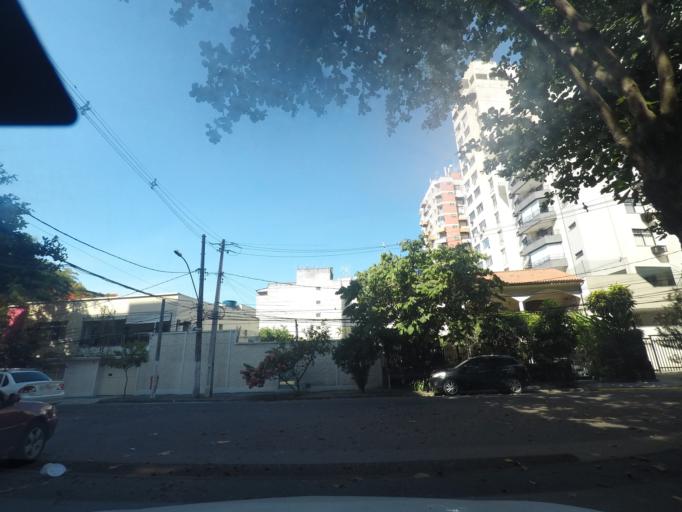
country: BR
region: Rio de Janeiro
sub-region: Niteroi
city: Niteroi
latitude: -22.9062
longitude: -43.1322
